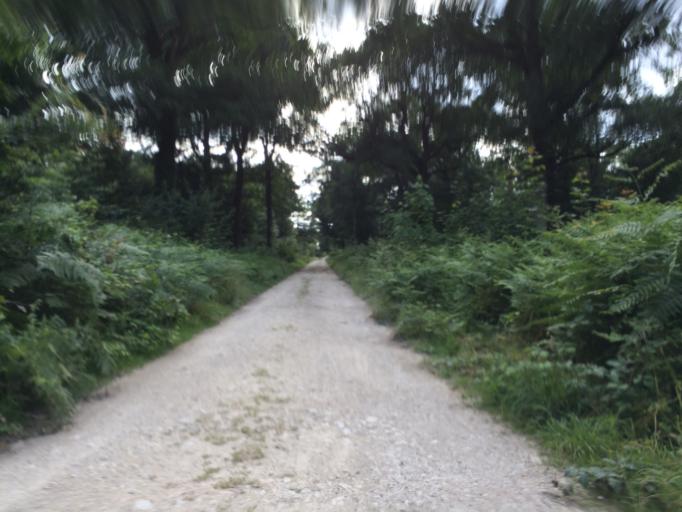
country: FR
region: Ile-de-France
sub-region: Departement de l'Essonne
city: Soisy-sur-Seine
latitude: 48.6622
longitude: 2.4401
